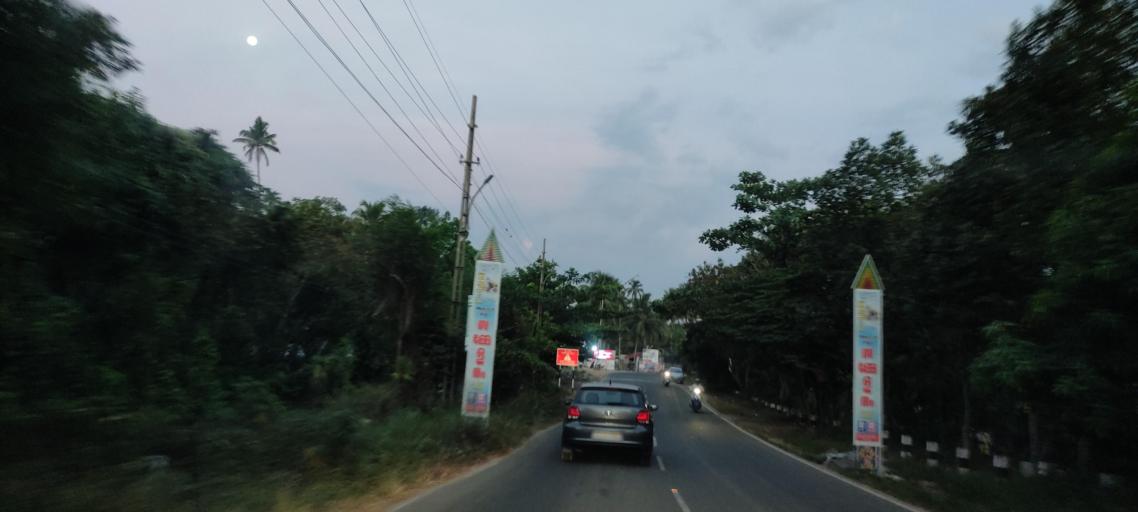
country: IN
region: Kerala
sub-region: Alappuzha
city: Kutiatodu
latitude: 9.7753
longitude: 76.3367
